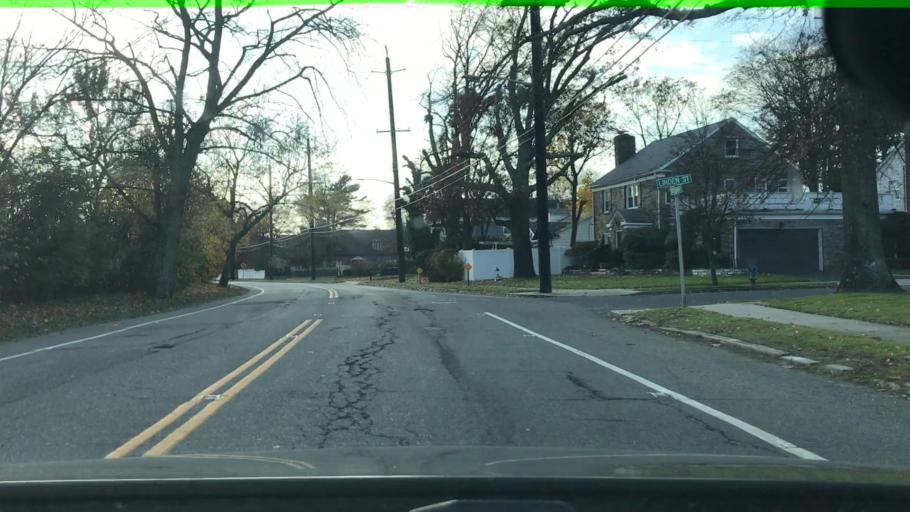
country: US
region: New York
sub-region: Nassau County
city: Woodmere
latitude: 40.6263
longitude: -73.7154
